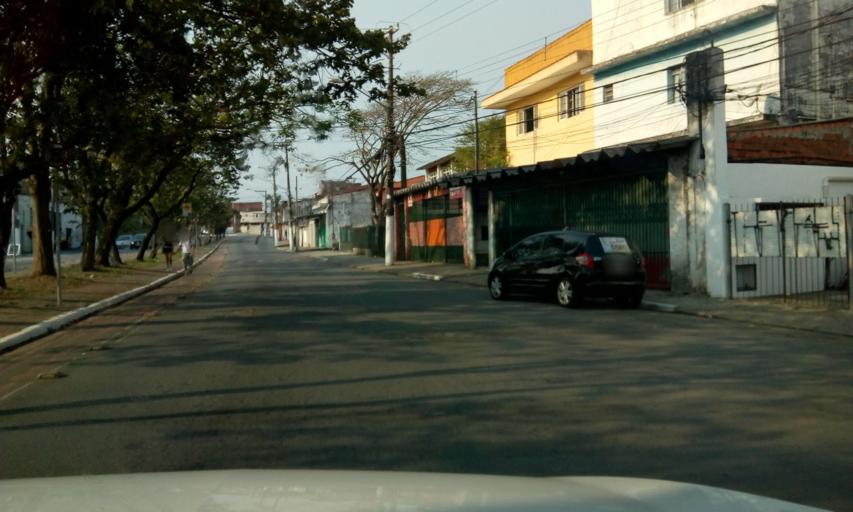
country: BR
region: Sao Paulo
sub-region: Diadema
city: Diadema
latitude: -23.7163
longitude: -46.6922
